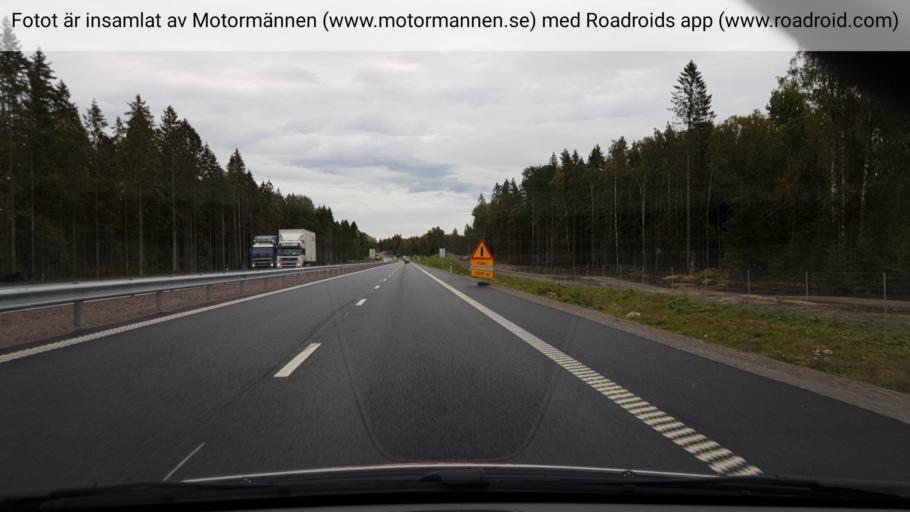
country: SE
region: Vaermland
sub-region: Hammaro Kommun
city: Skoghall
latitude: 59.3822
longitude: 13.3730
